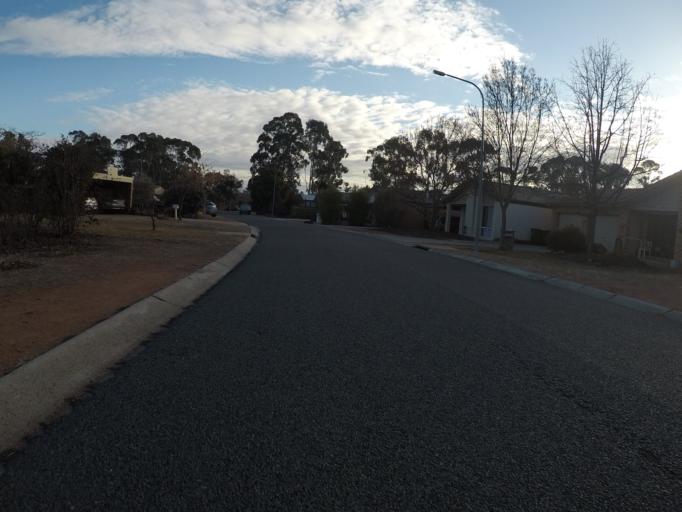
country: AU
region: Australian Capital Territory
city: Macarthur
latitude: -35.4248
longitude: 149.0977
